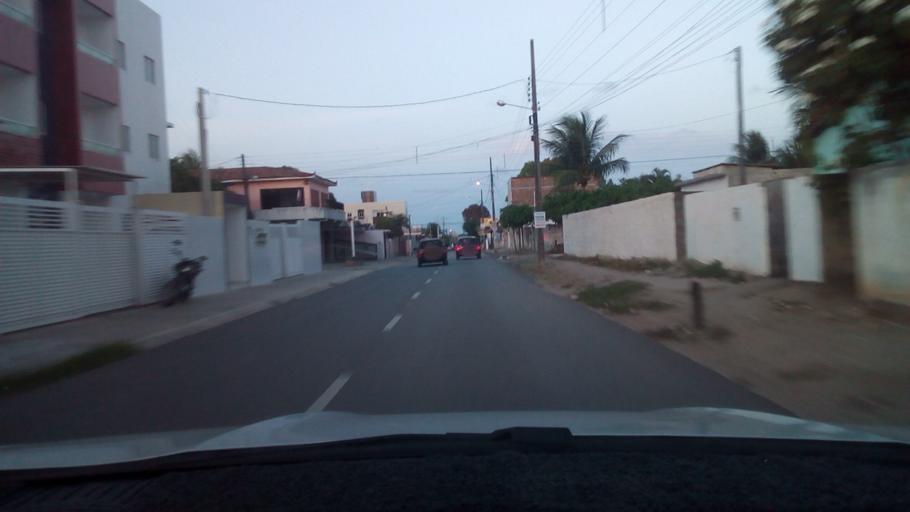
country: BR
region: Paraiba
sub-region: Bayeux
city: Bayeux
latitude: -7.1777
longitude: -34.9193
